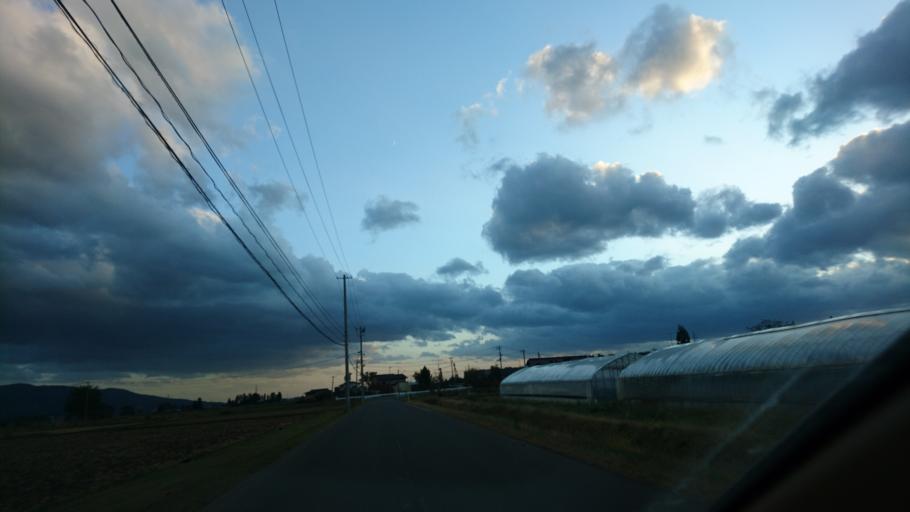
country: JP
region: Iwate
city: Mizusawa
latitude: 39.0974
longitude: 141.1454
